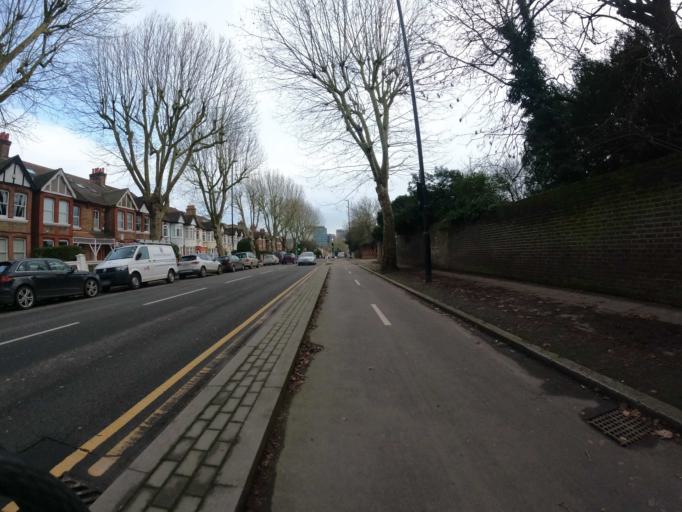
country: GB
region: England
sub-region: Greater London
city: Brentford
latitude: 51.4929
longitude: -0.3185
